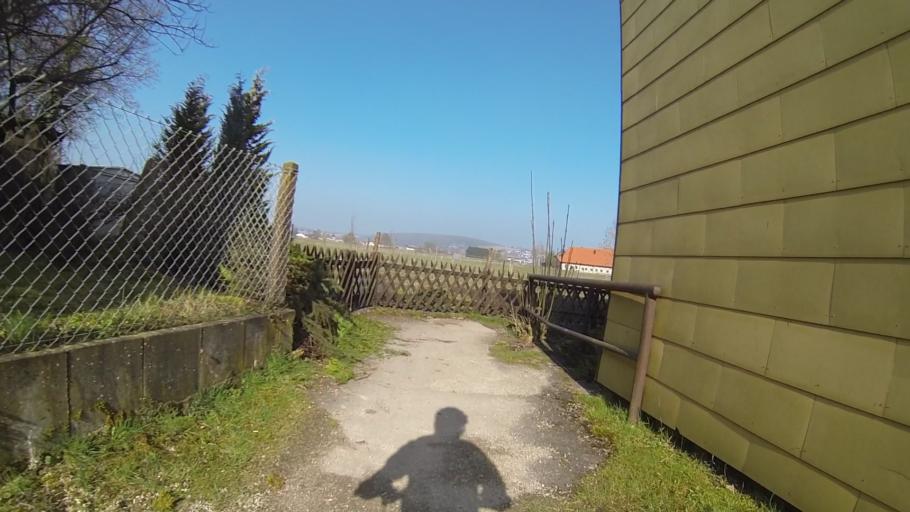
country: DE
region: Baden-Wuerttemberg
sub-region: Regierungsbezirk Stuttgart
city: Bolheim
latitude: 48.6181
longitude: 10.1510
